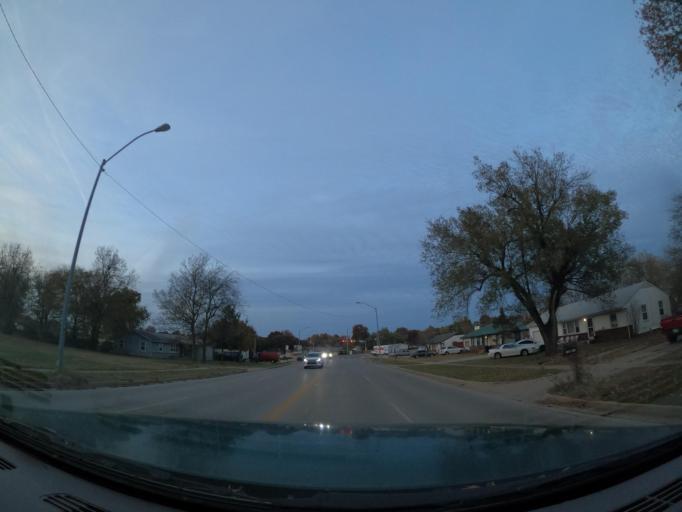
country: US
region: Oklahoma
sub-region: Tulsa County
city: Broken Arrow
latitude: 36.0598
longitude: -95.7908
